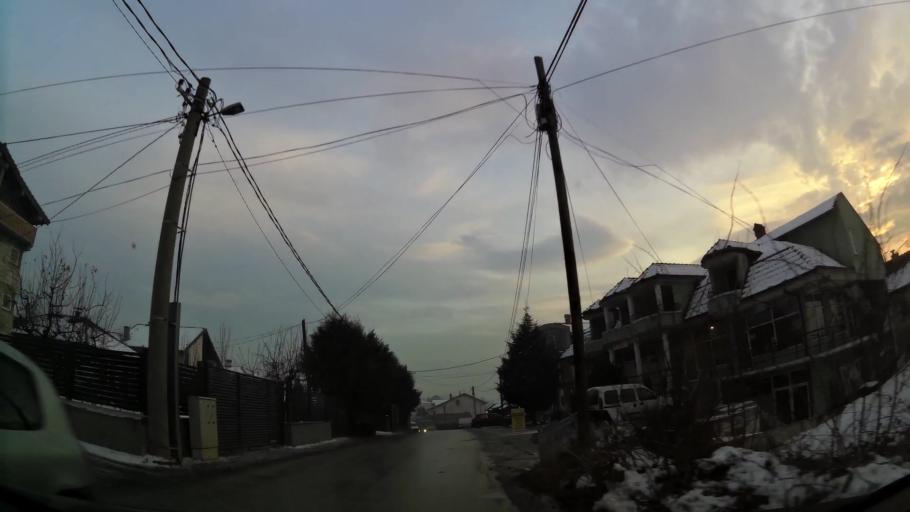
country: MK
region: Suto Orizari
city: Suto Orizare
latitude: 42.0373
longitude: 21.4100
